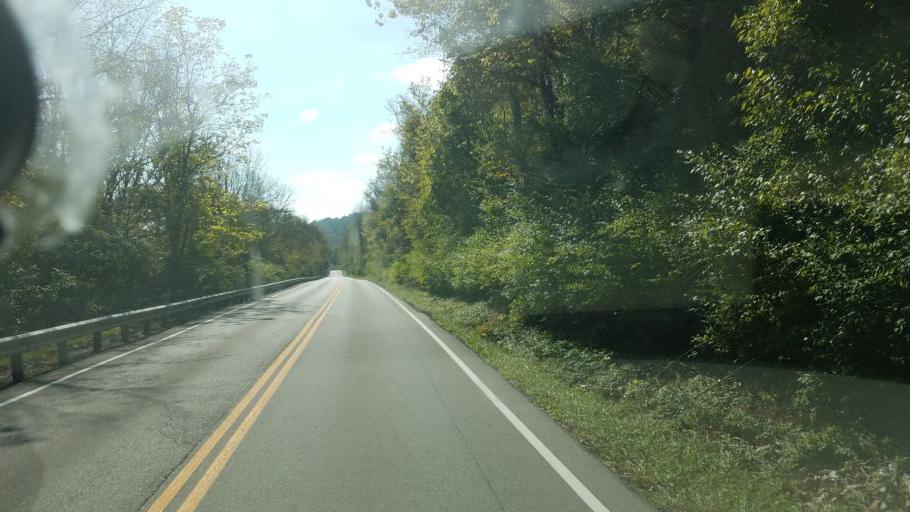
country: US
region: Ohio
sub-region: Brown County
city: Aberdeen
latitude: 38.6676
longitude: -83.7814
